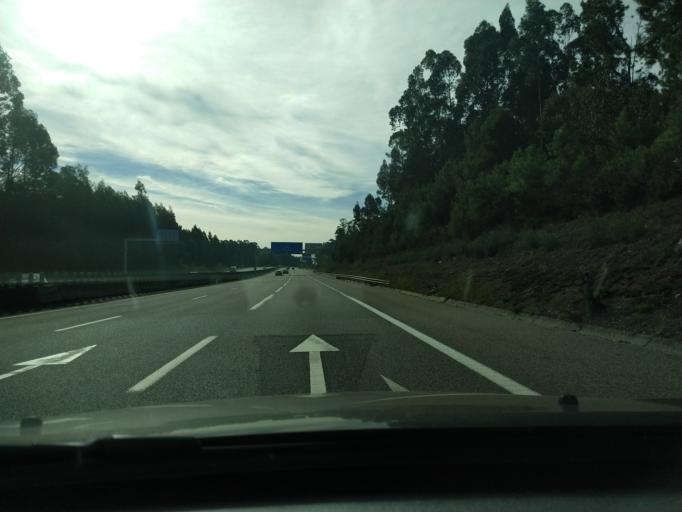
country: PT
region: Aveiro
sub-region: Santa Maria da Feira
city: Rio Meao
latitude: 40.9356
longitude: -8.5726
